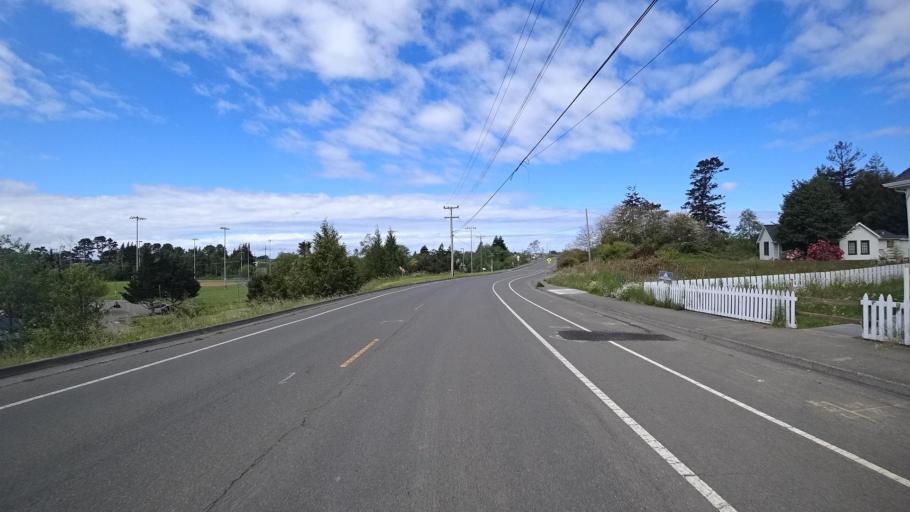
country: US
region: California
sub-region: Humboldt County
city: Arcata
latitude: 40.8665
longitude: -124.0795
